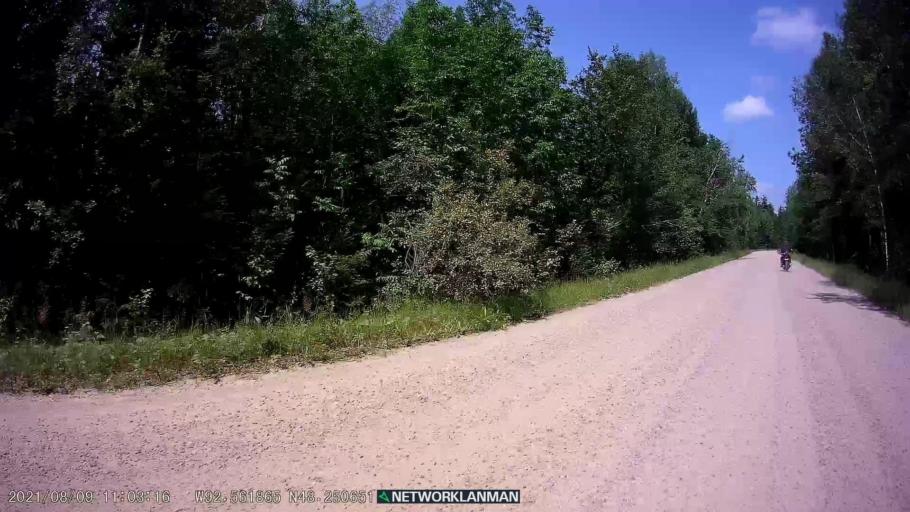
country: US
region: Minnesota
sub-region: Saint Louis County
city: Parkville
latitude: 48.2508
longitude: -92.5619
